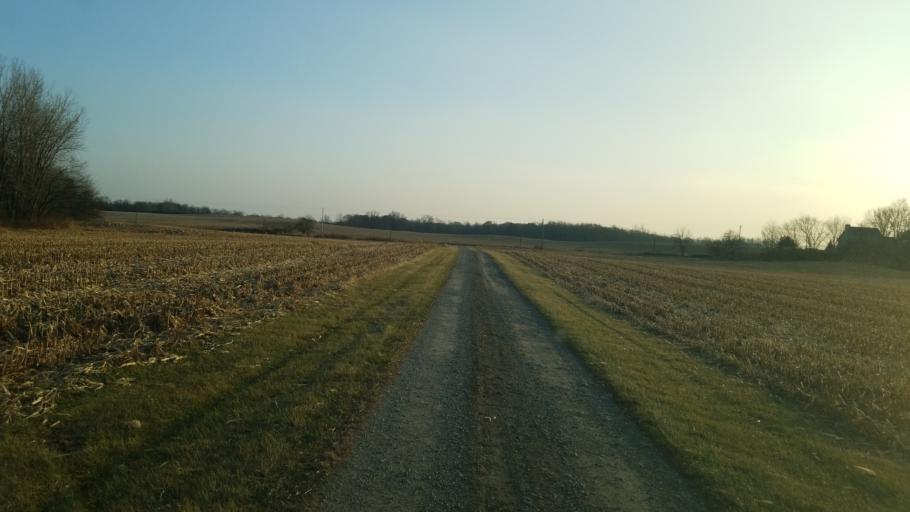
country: US
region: Ohio
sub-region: Knox County
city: Centerburg
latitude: 40.3191
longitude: -82.6418
